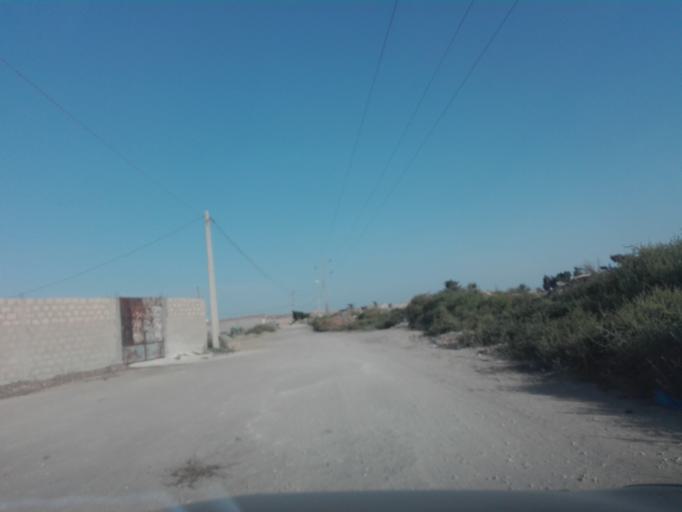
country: TN
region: Qabis
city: Gabes
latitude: 33.9591
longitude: 10.0620
